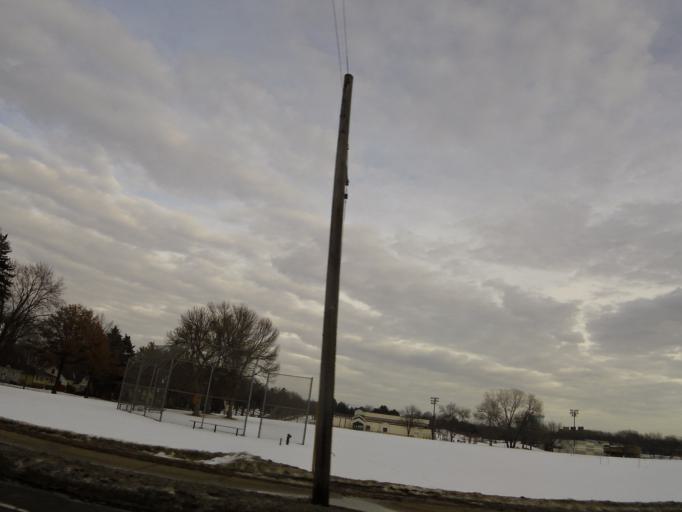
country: US
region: Minnesota
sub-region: Ramsey County
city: Maplewood
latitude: 44.9555
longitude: -93.0152
